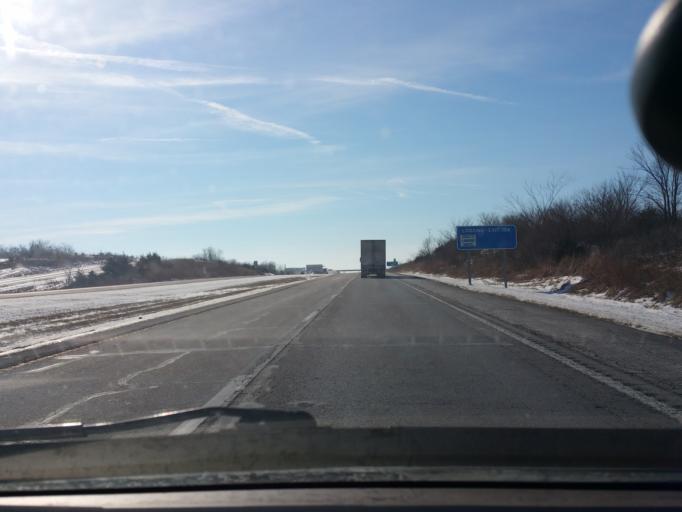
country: US
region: Iowa
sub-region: Decatur County
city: Lamoni
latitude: 40.4780
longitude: -93.9739
